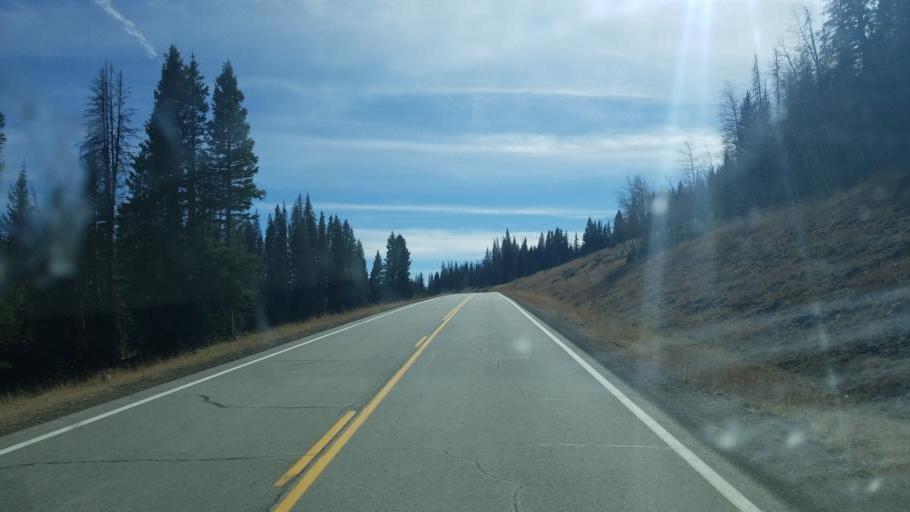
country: US
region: New Mexico
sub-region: Rio Arriba County
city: Chama
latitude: 37.0368
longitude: -106.4119
